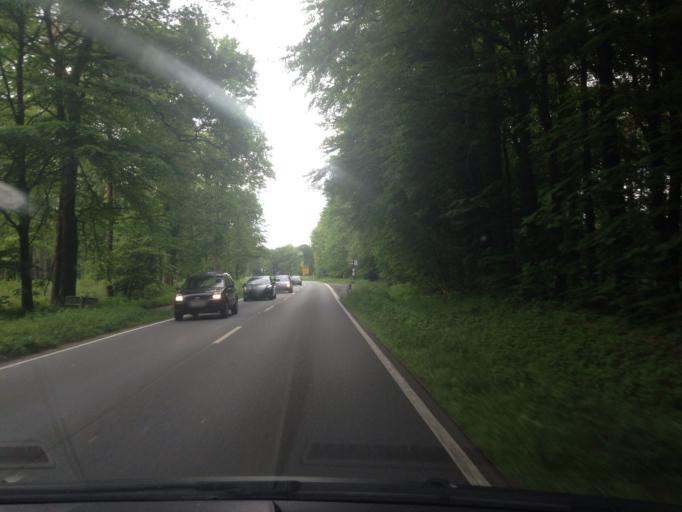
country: DE
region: North Rhine-Westphalia
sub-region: Regierungsbezirk Munster
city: Senden
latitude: 51.8787
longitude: 7.4963
